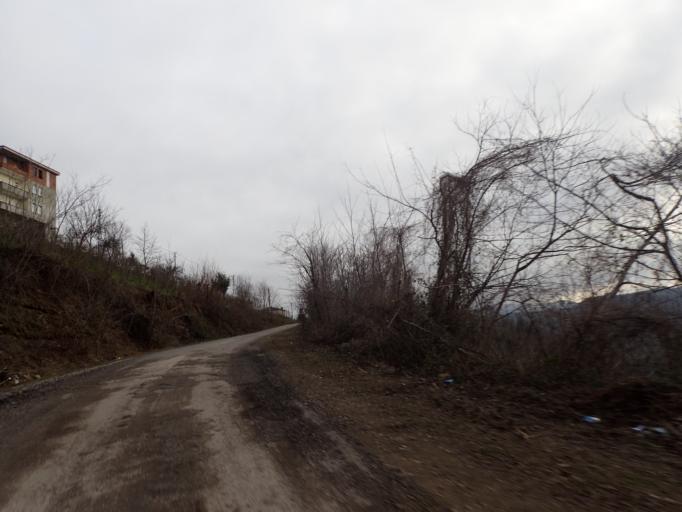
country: TR
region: Ordu
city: Camas
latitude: 40.9394
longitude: 37.5175
